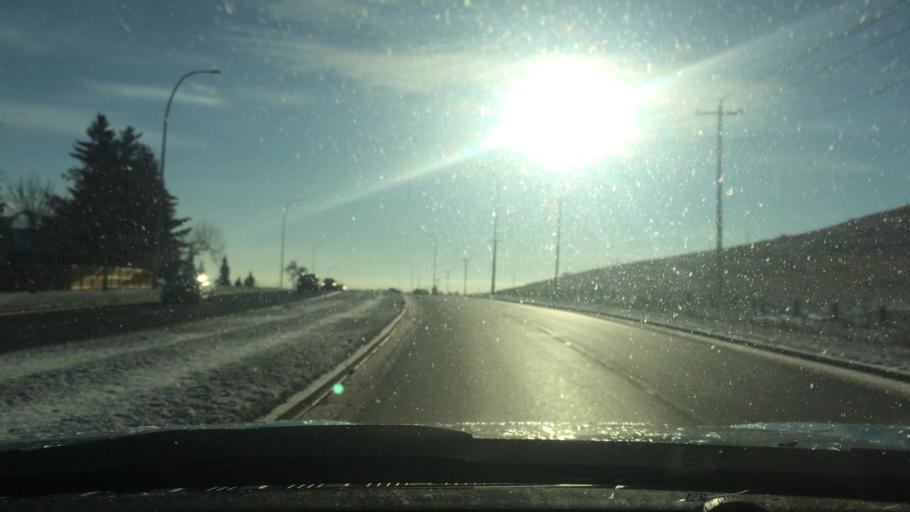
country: CA
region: Alberta
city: Calgary
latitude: 51.1279
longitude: -114.1037
